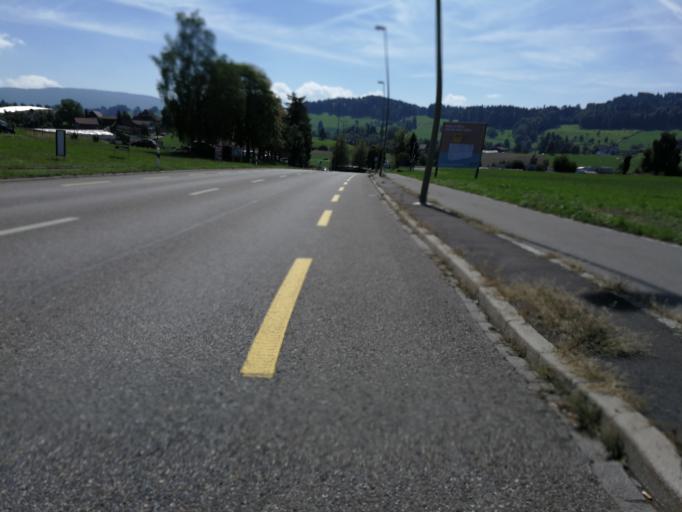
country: CH
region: Zurich
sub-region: Bezirk Horgen
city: Au
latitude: 47.2334
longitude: 8.6352
